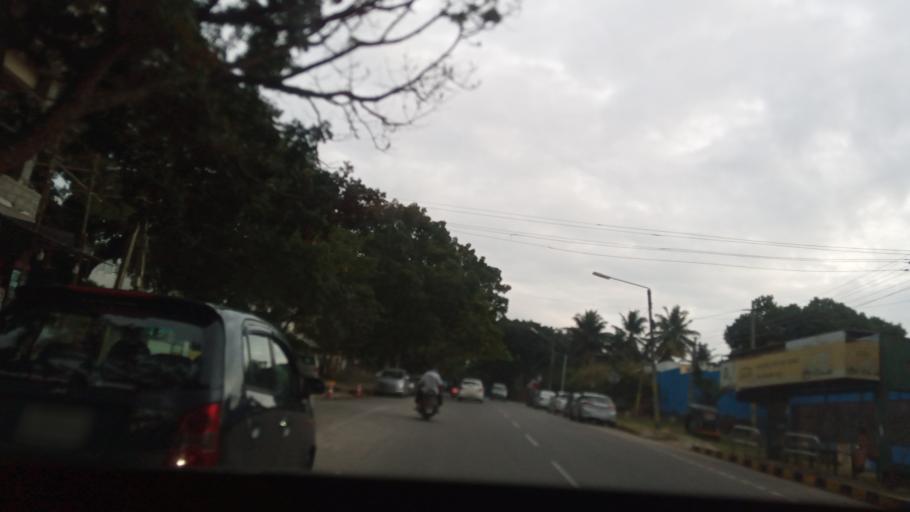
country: IN
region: Karnataka
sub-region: Mysore
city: Mysore
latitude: 12.3292
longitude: 76.6301
